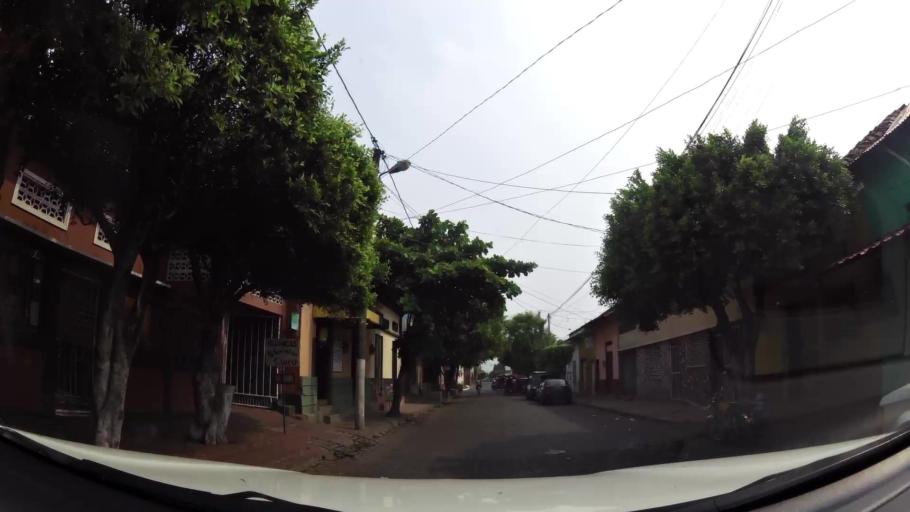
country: NI
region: Chinandega
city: Chinandega
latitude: 12.6297
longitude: -87.1273
